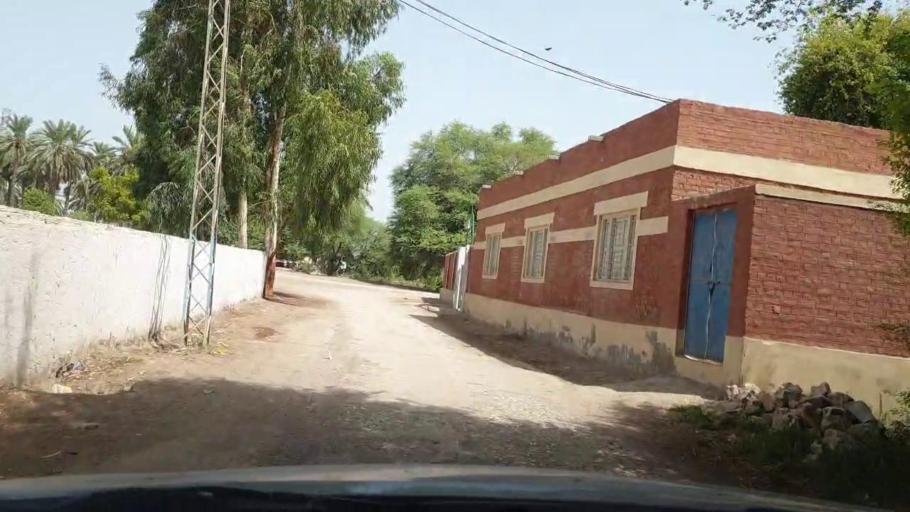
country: PK
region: Sindh
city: Pano Aqil
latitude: 27.9087
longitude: 69.1517
